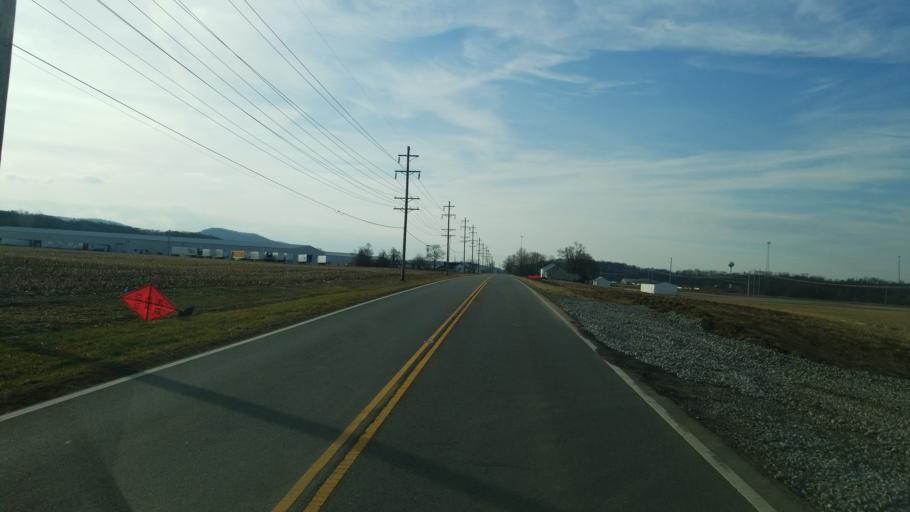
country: US
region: Ohio
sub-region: Ross County
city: Kingston
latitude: 39.4197
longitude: -82.9558
